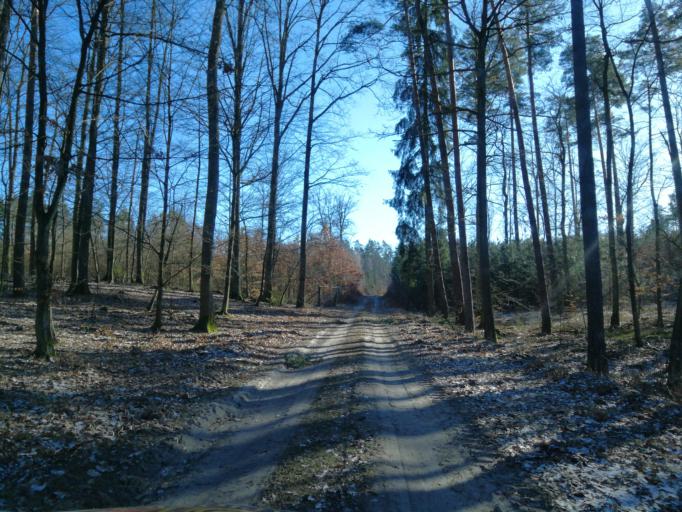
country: PL
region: Kujawsko-Pomorskie
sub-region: Powiat brodnicki
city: Gorzno
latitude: 53.2187
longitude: 19.7099
